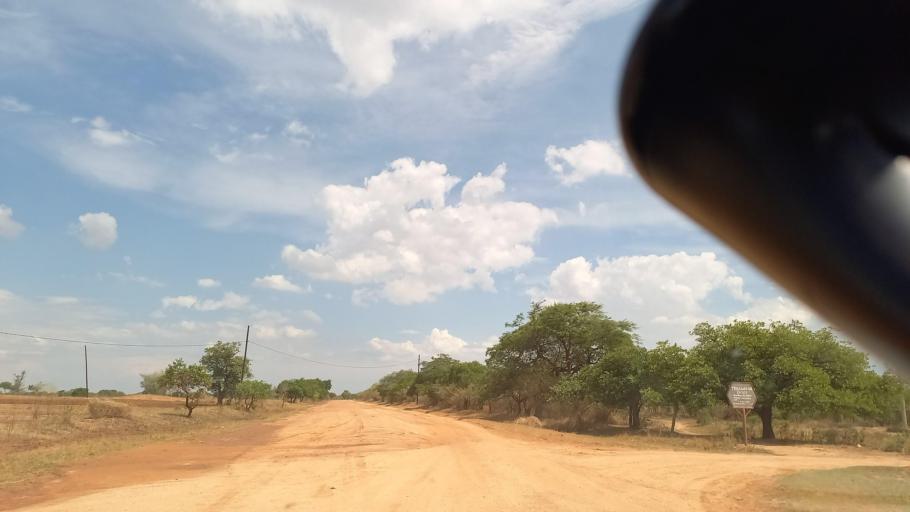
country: ZM
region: Lusaka
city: Kafue
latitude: -16.1156
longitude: 28.0331
